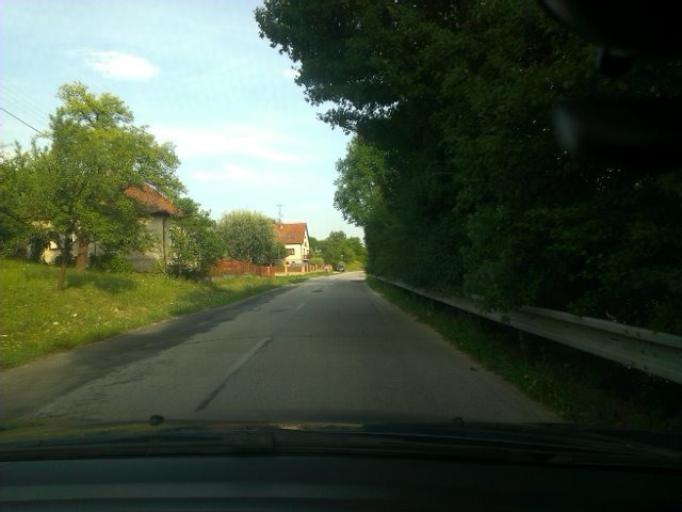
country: SK
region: Trenciansky
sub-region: Okres Myjava
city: Myjava
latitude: 48.7782
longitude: 17.5748
